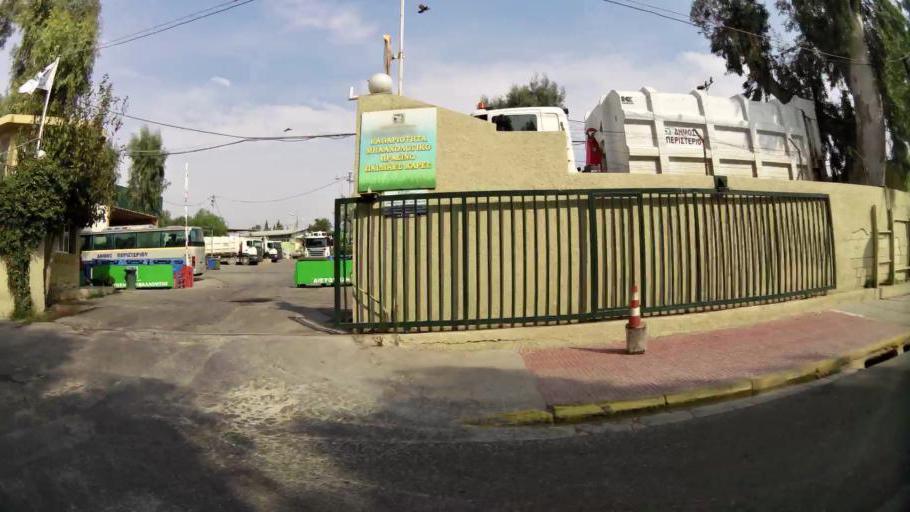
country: GR
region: Attica
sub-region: Nomarchia Athinas
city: Peristeri
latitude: 38.0178
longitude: 23.6863
